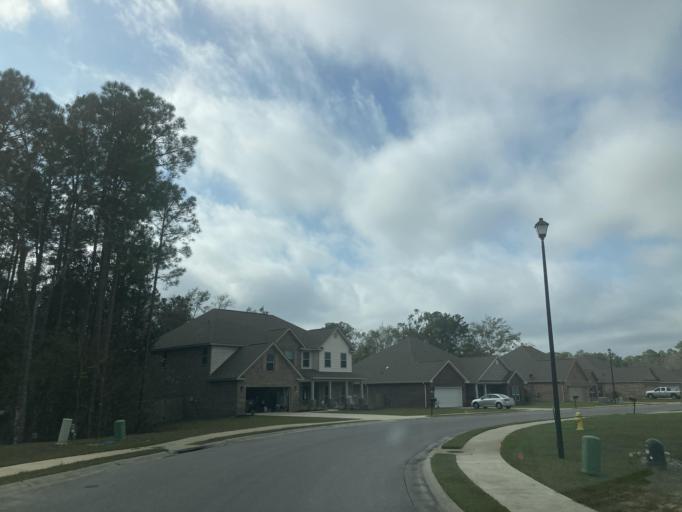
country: US
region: Mississippi
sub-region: Harrison County
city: D'Iberville
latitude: 30.4765
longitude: -88.9813
